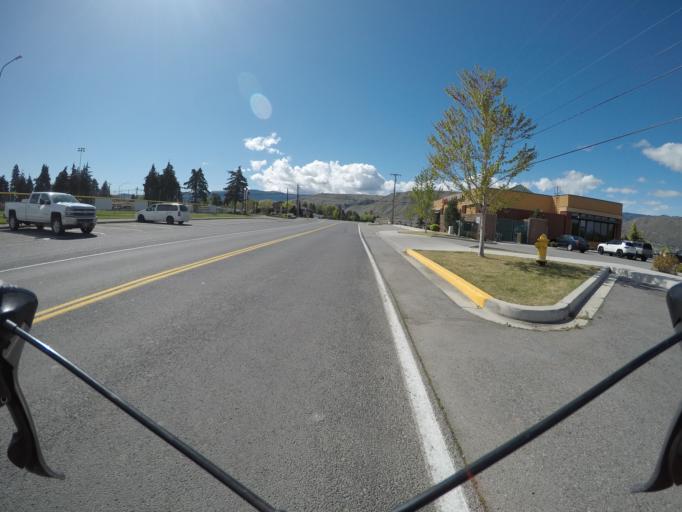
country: US
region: Washington
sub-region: Douglas County
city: East Wenatchee
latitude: 47.4067
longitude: -120.2772
